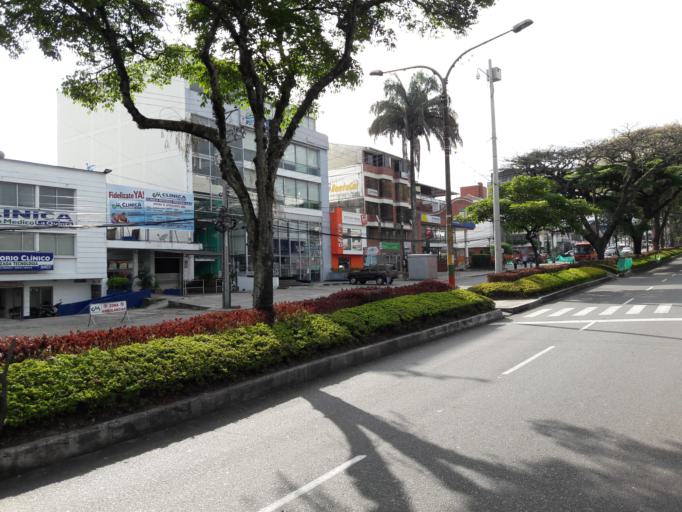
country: CO
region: Tolima
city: Ibague
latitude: 4.4362
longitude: -75.2134
